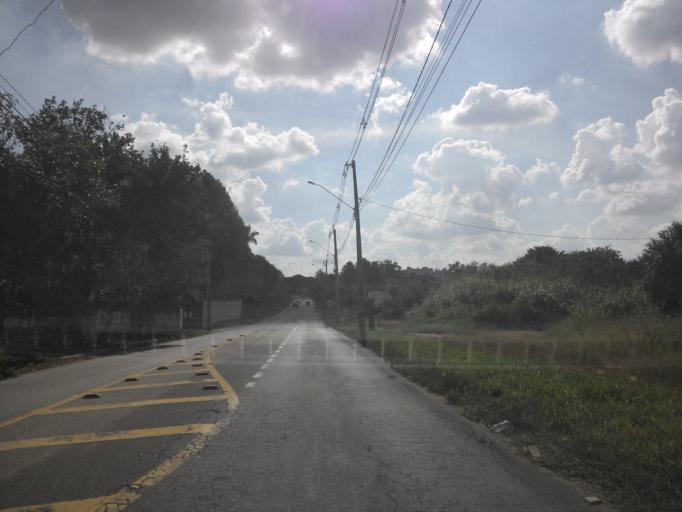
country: BR
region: Sao Paulo
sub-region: Valinhos
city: Valinhos
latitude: -22.9908
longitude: -47.0073
